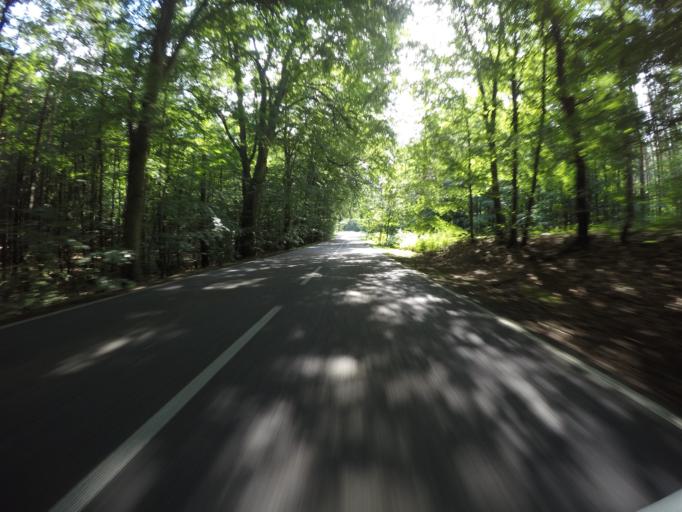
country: DE
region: Brandenburg
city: Rheinsberg
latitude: 53.1109
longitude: 12.9998
